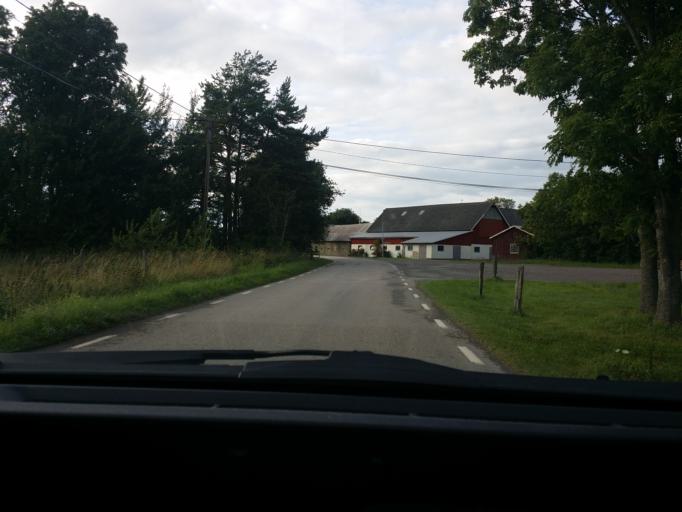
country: SE
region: Kalmar
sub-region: Borgholms Kommun
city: Borgholm
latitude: 57.1176
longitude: 16.9663
